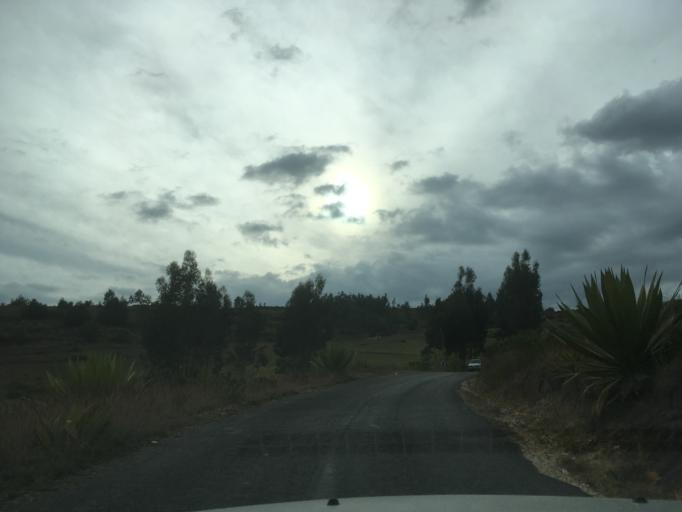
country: CO
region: Boyaca
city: Firavitoba
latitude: 5.6732
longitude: -73.0132
